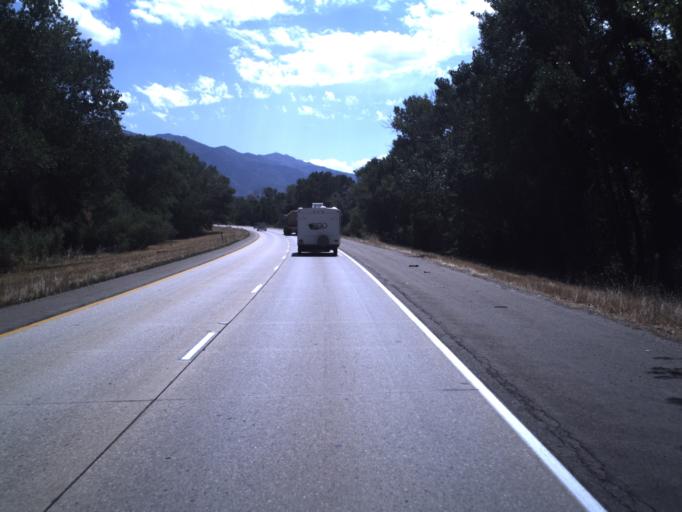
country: US
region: Utah
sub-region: Weber County
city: Riverdale
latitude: 41.1587
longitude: -111.9931
